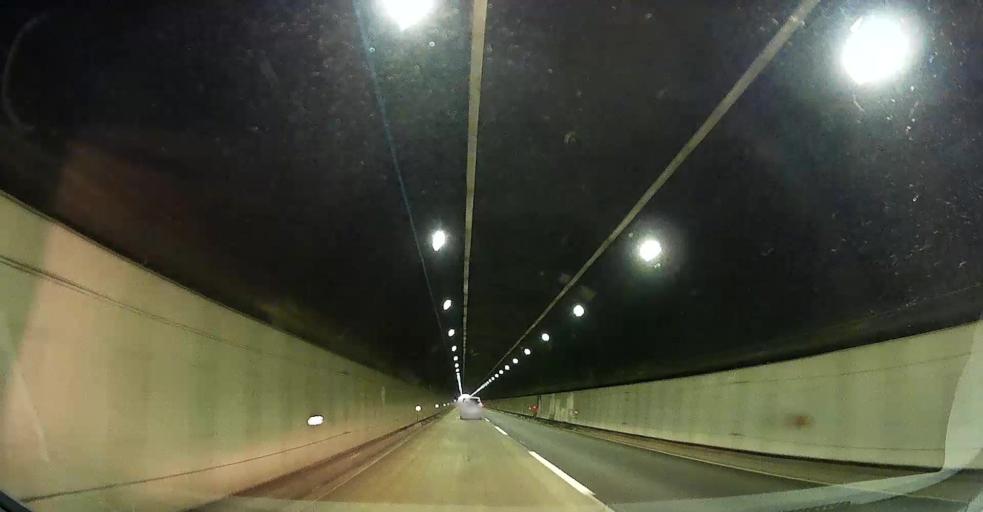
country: JP
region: Kanagawa
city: Ninomiya
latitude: 35.2948
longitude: 139.2098
